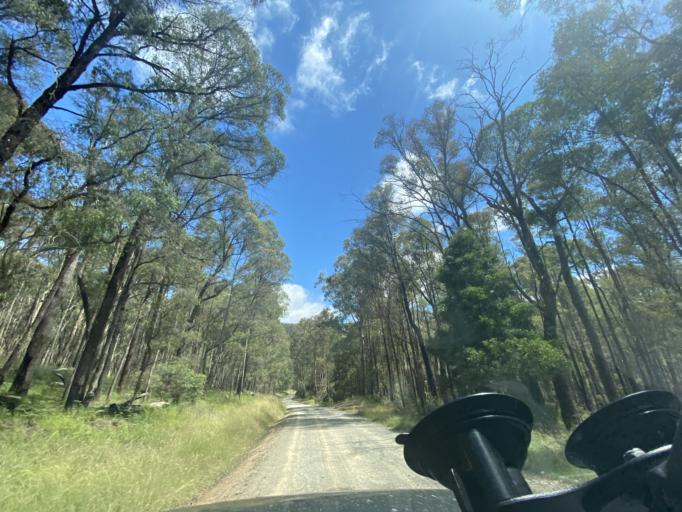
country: AU
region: Victoria
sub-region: Yarra Ranges
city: Millgrove
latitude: -37.5310
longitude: 146.0061
